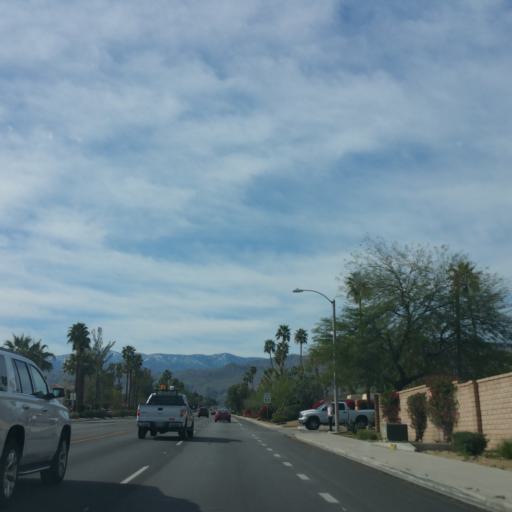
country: US
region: California
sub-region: Riverside County
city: Palm Desert
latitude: 33.7171
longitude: -116.3919
